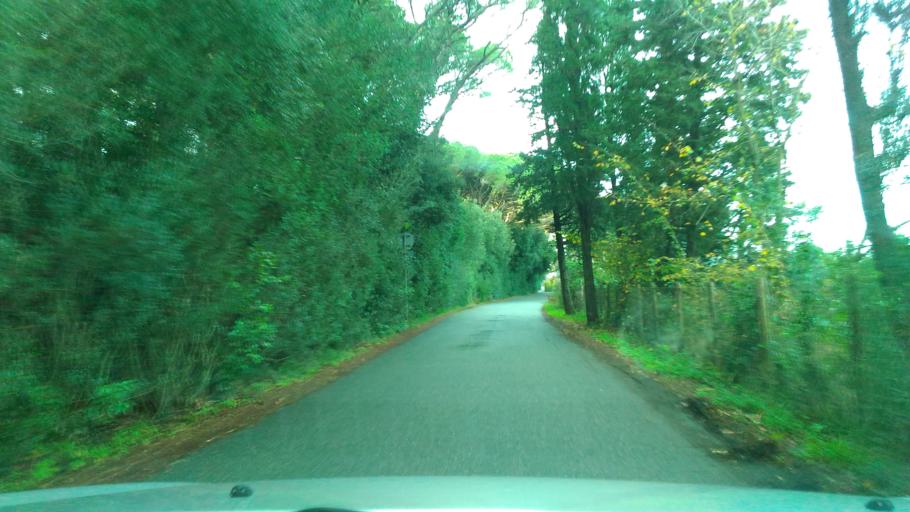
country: IT
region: Tuscany
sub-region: Provincia di Livorno
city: Cecina
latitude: 43.2847
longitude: 10.5116
